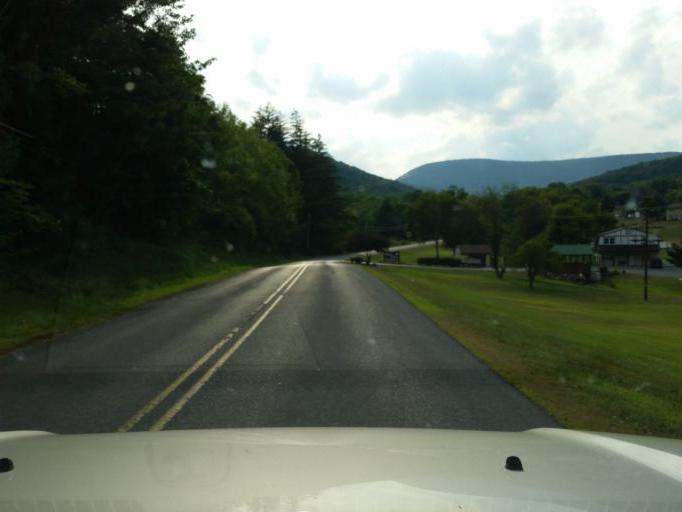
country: US
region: Pennsylvania
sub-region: Blair County
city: Duncansville
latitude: 40.4310
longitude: -78.4538
